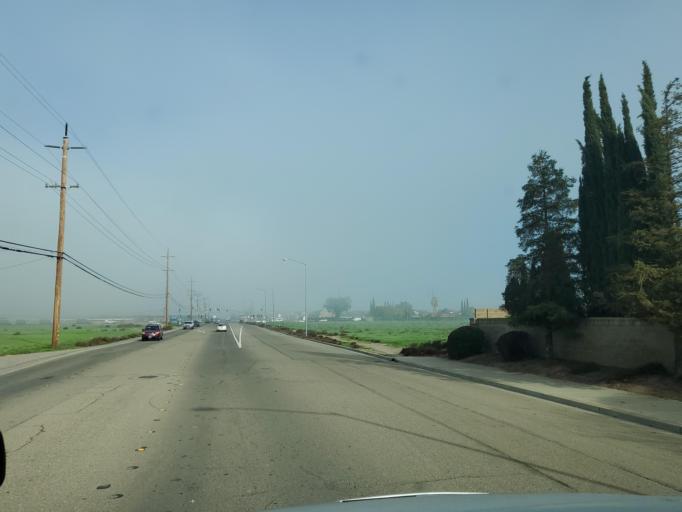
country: US
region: California
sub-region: San Joaquin County
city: Lathrop
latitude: 37.8091
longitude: -121.2529
